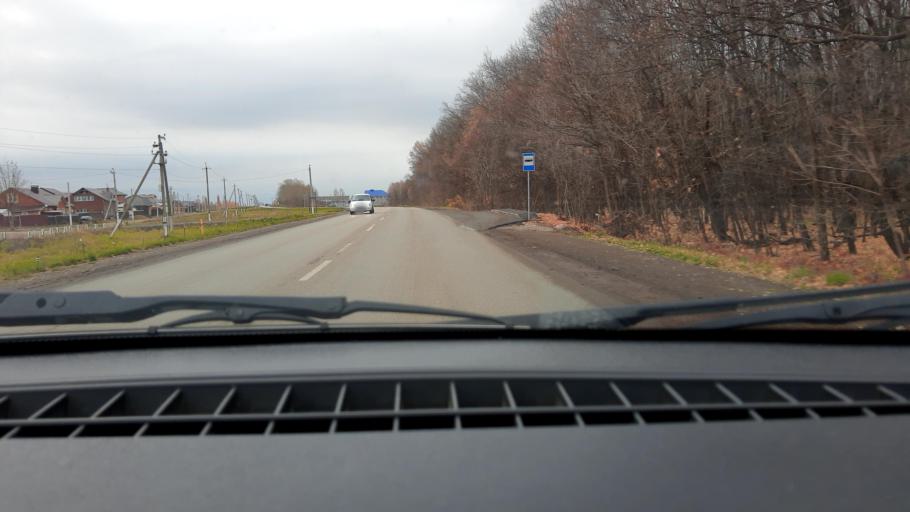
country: RU
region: Bashkortostan
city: Mikhaylovka
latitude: 54.8254
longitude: 55.8827
